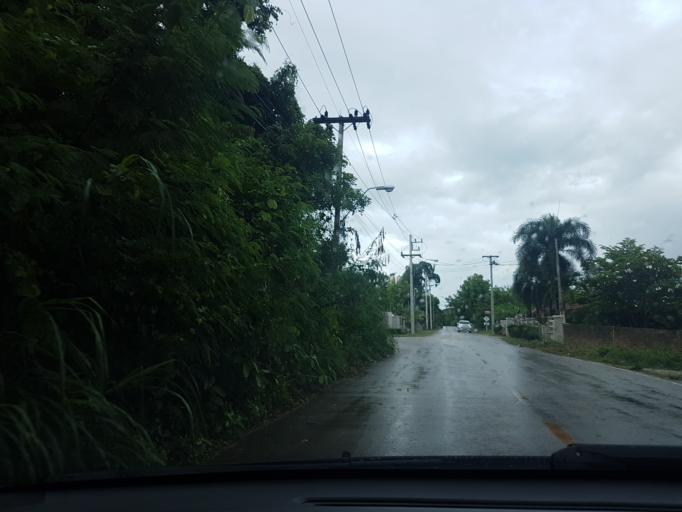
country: TH
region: Lampang
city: Lampang
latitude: 18.2989
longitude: 99.4742
